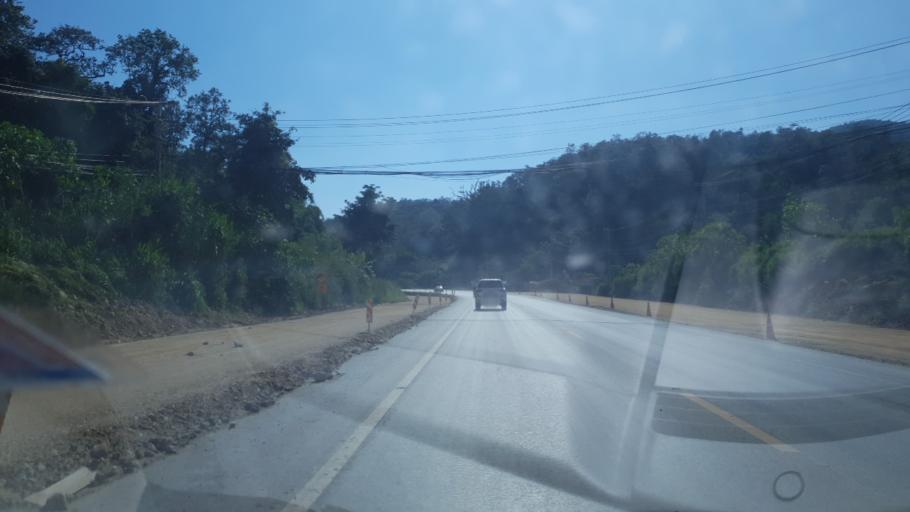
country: TH
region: Chiang Mai
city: Mae On
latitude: 19.0372
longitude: 99.3265
